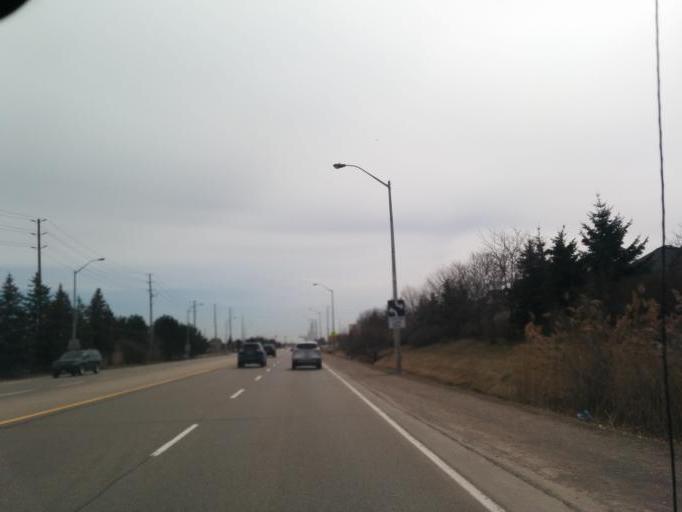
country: CA
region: Ontario
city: Brampton
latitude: 43.7275
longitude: -79.8165
